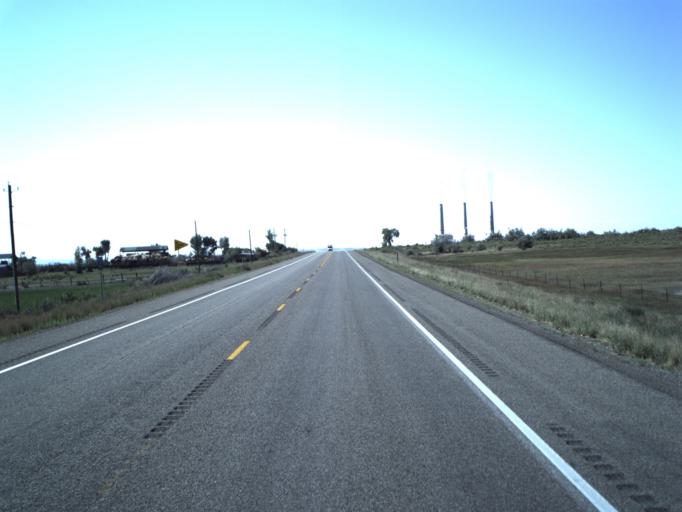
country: US
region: Utah
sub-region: Emery County
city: Castle Dale
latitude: 39.2019
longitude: -111.0242
